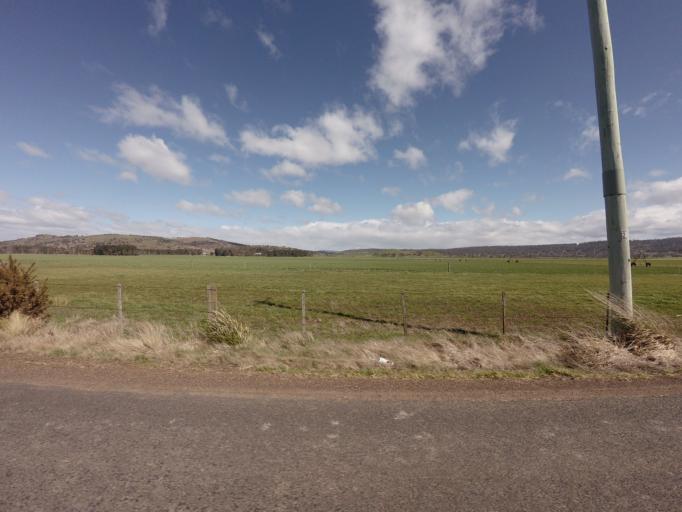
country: AU
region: Tasmania
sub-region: Northern Midlands
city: Evandale
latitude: -42.0227
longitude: 147.4720
